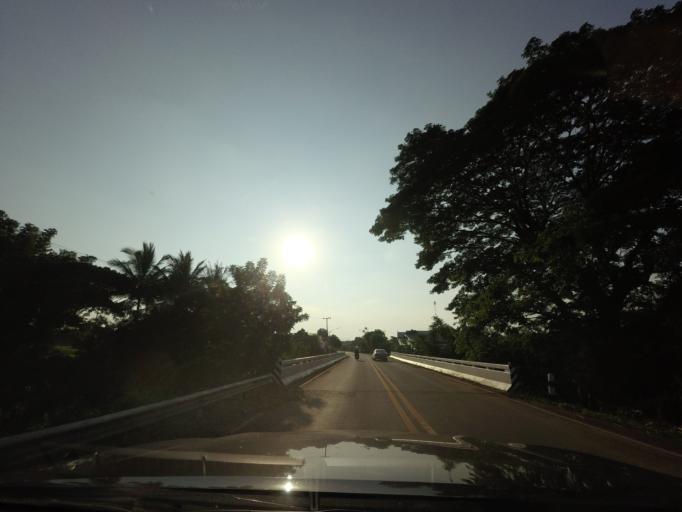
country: TH
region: Nan
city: Na Noi
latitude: 18.3353
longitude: 100.7534
